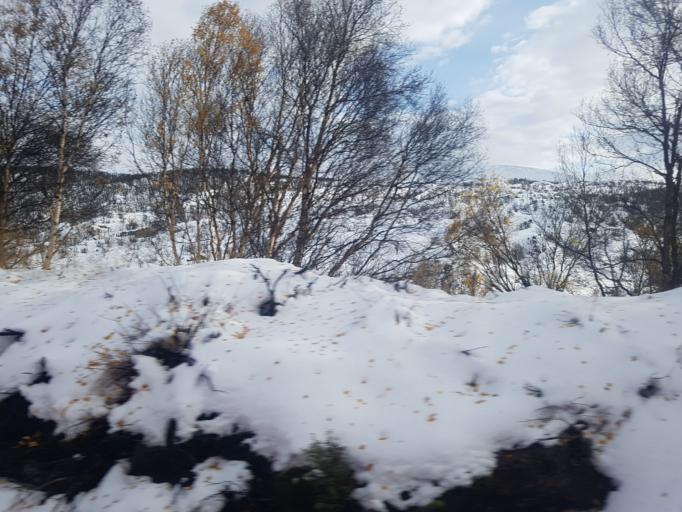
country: NO
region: Sor-Trondelag
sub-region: Oppdal
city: Oppdal
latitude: 62.2883
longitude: 9.5975
